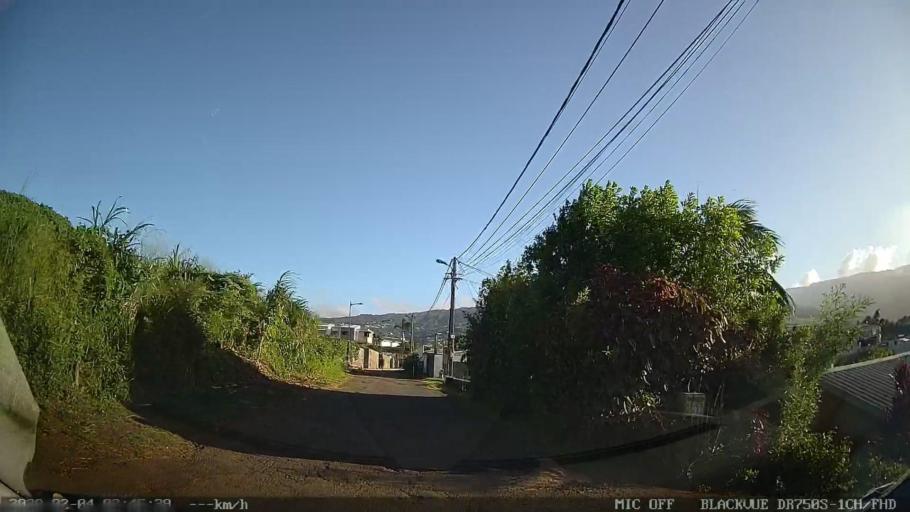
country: RE
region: Reunion
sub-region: Reunion
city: Sainte-Marie
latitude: -20.9201
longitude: 55.5249
